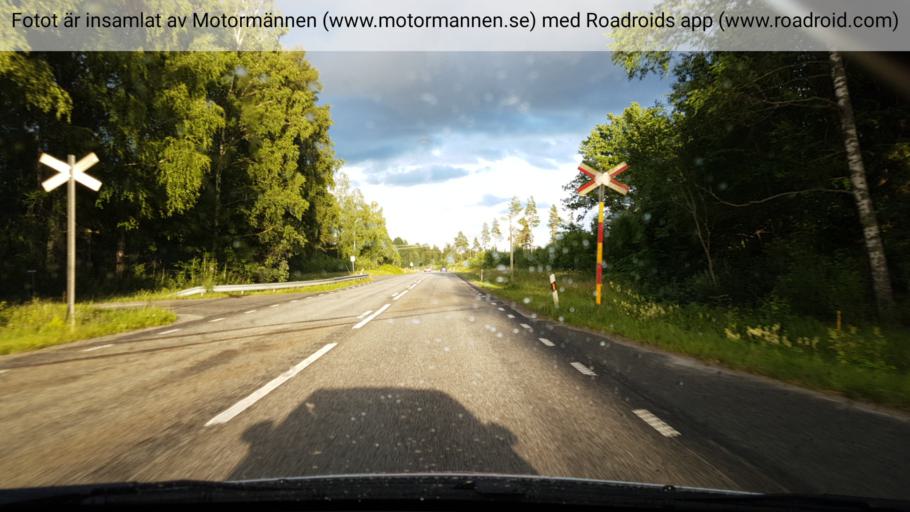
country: SE
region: OErebro
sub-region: Nora Kommun
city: Nora
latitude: 59.4801
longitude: 15.0883
